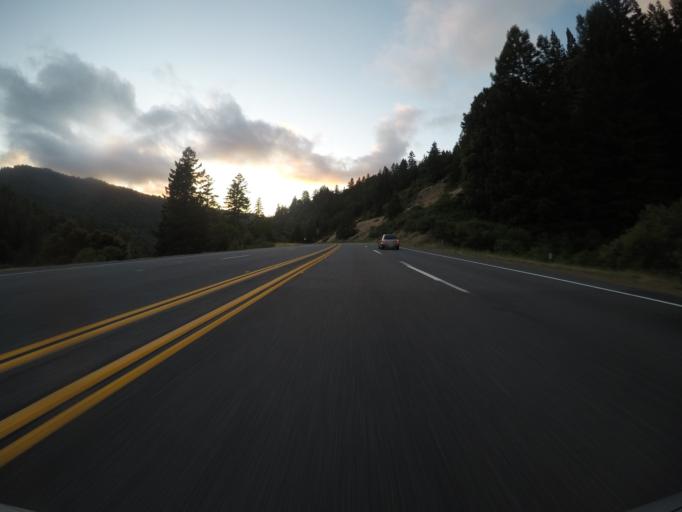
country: US
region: California
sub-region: Humboldt County
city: Redway
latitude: 40.0448
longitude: -123.7823
